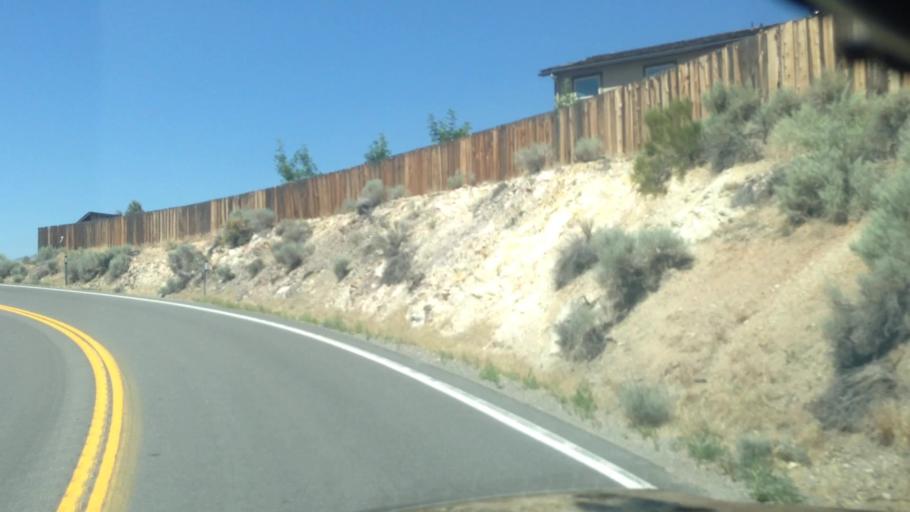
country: US
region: Nevada
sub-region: Storey County
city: Virginia City
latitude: 39.3867
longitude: -119.7152
